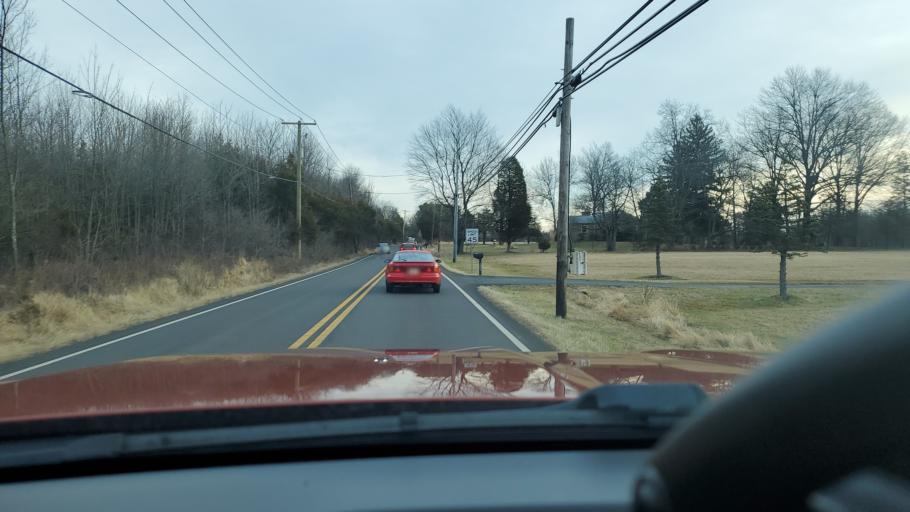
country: US
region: Pennsylvania
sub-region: Montgomery County
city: Telford
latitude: 40.3547
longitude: -75.3629
